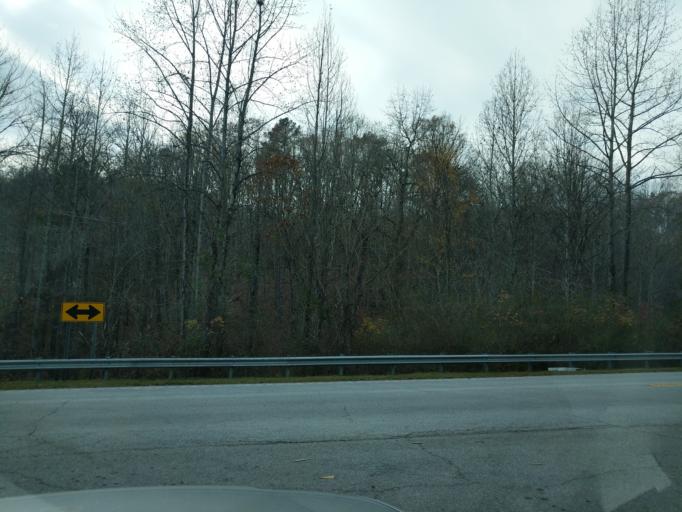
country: US
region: South Carolina
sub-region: Oconee County
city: Utica
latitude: 34.7763
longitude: -82.8960
